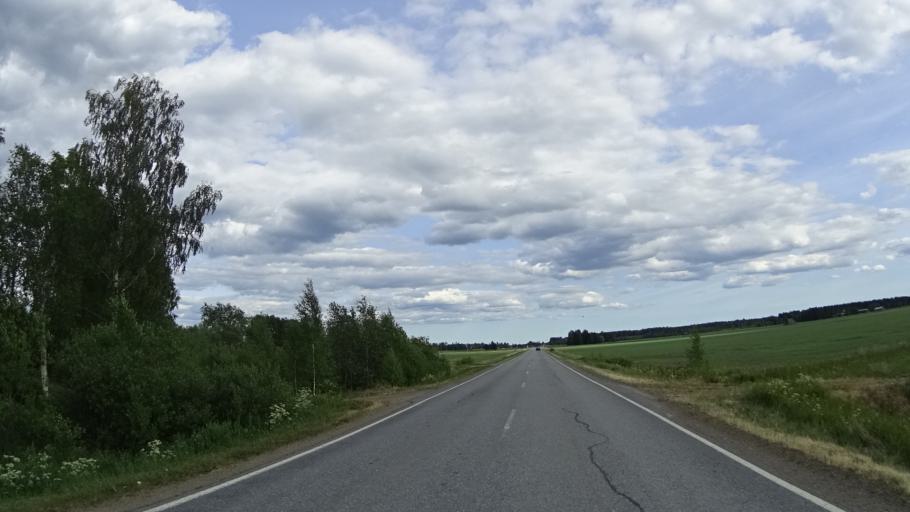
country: FI
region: Pirkanmaa
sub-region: Etelae-Pirkanmaa
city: Urjala
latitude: 60.9516
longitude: 23.5310
